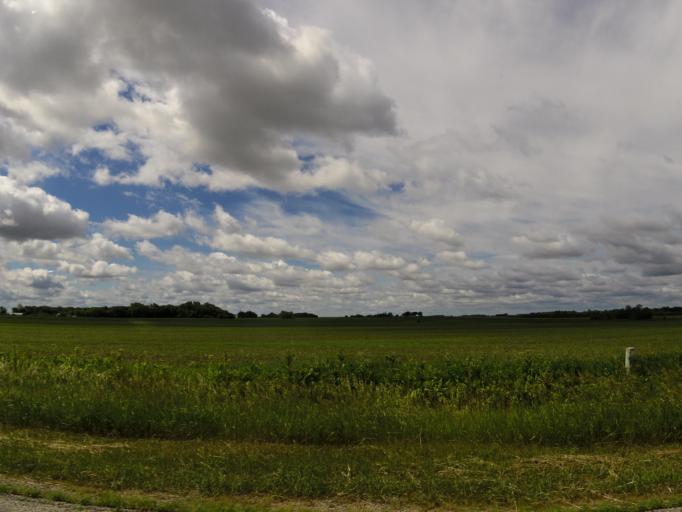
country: US
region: Minnesota
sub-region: Fillmore County
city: Spring Valley
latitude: 43.7107
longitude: -92.4216
